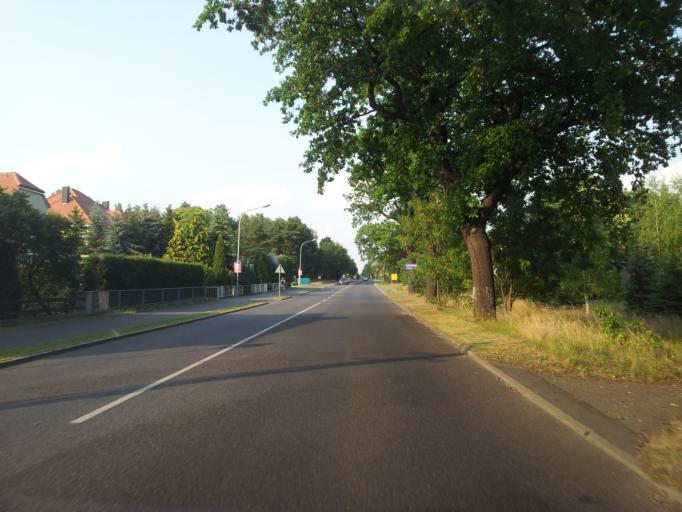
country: DE
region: Saxony
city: Bernsdorf
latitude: 51.3797
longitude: 14.0763
